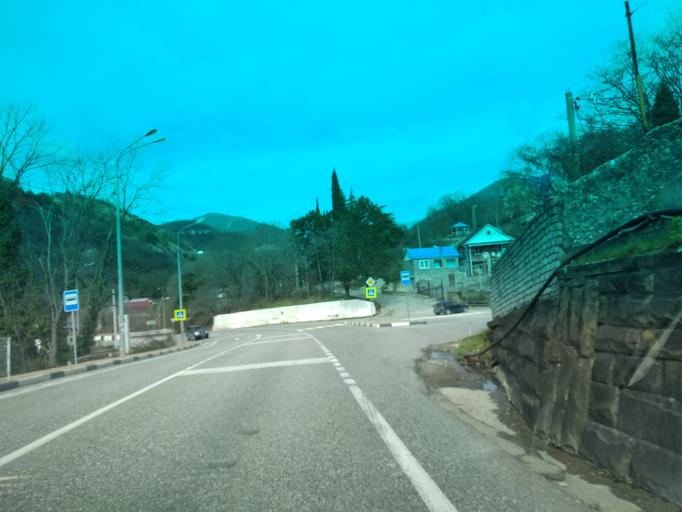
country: RU
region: Krasnodarskiy
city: Shepsi
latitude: 44.0574
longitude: 39.1350
